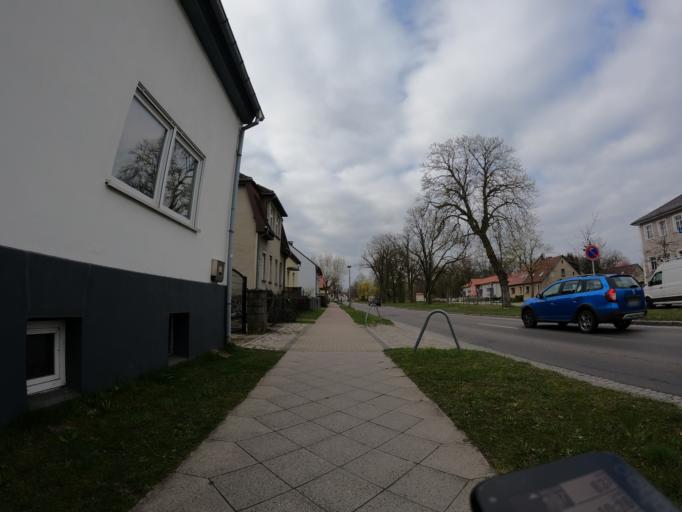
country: DE
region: Brandenburg
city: Neuenhagen
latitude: 52.5345
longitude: 13.6961
